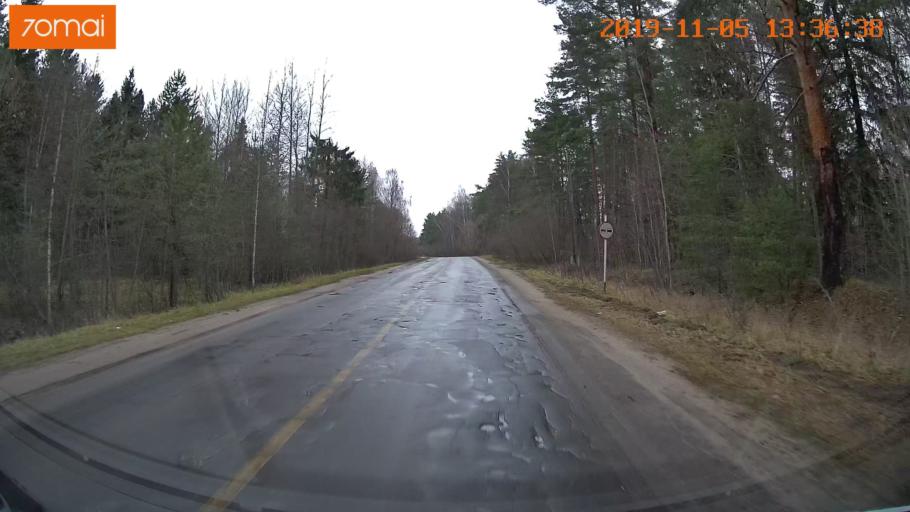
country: RU
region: Ivanovo
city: Shuya
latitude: 56.9160
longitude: 41.3823
